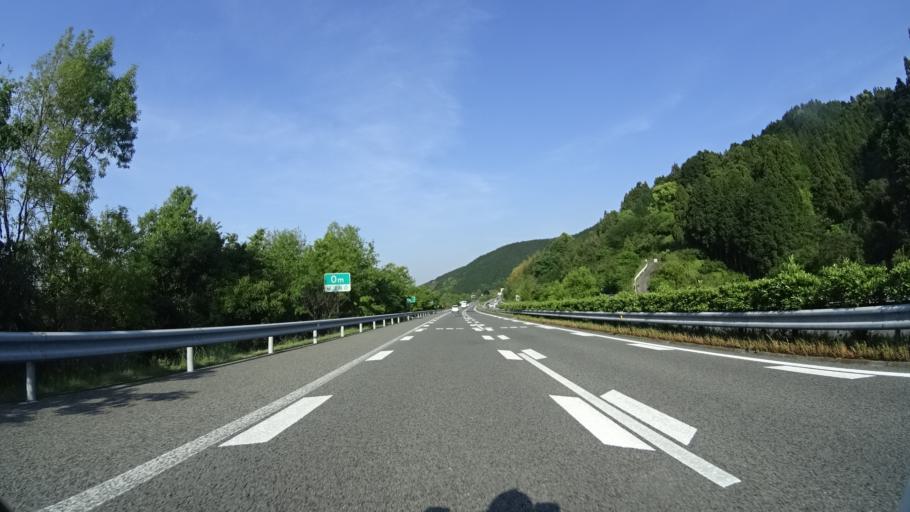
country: JP
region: Ehime
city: Saijo
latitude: 33.8856
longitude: 133.1383
